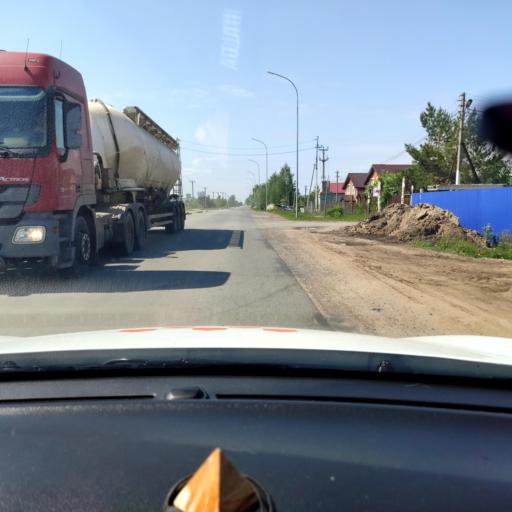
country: RU
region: Tatarstan
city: Stolbishchi
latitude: 55.6957
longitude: 49.1962
